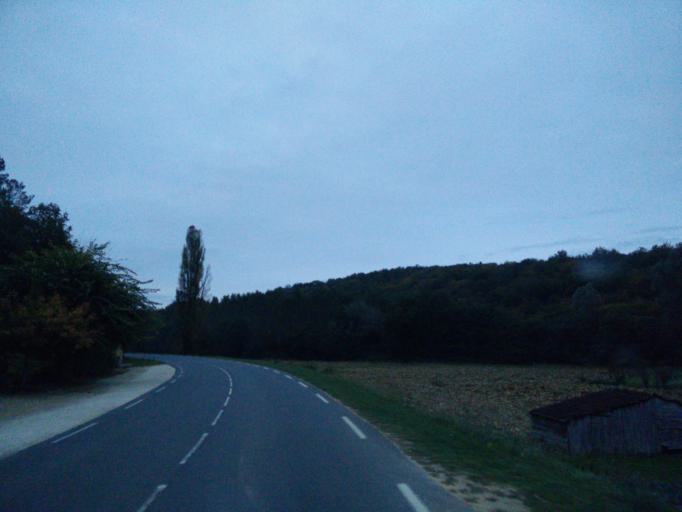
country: FR
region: Aquitaine
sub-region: Departement de la Dordogne
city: Saint-Cyprien
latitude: 44.9150
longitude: 1.1082
